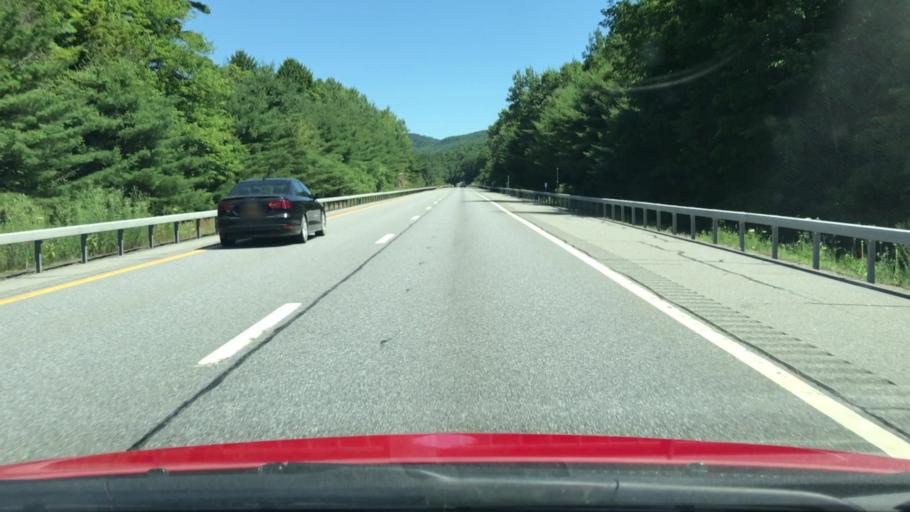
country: US
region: New York
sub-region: Warren County
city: Warrensburg
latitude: 43.5375
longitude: -73.7386
